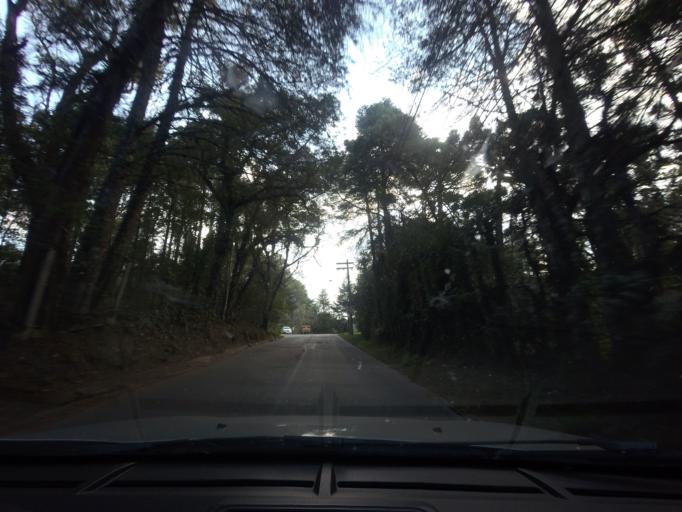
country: BR
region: Sao Paulo
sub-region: Campos Do Jordao
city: Campos do Jordao
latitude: -22.7408
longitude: -45.5678
